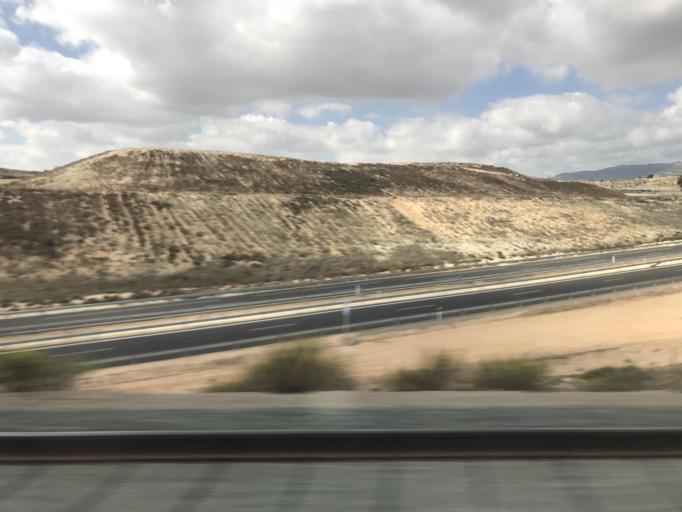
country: ES
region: Castille-La Mancha
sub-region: Provincia de Albacete
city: Caudete
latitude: 38.7225
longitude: -0.9334
